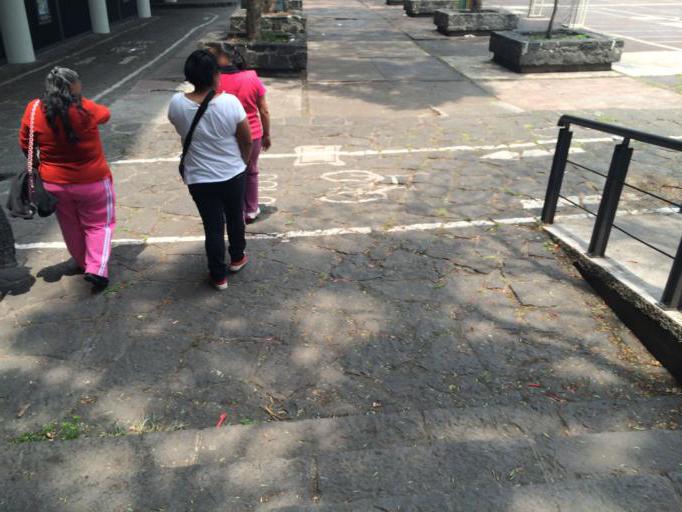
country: MX
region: Mexico City
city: Coyoacan
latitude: 19.3317
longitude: -99.1820
